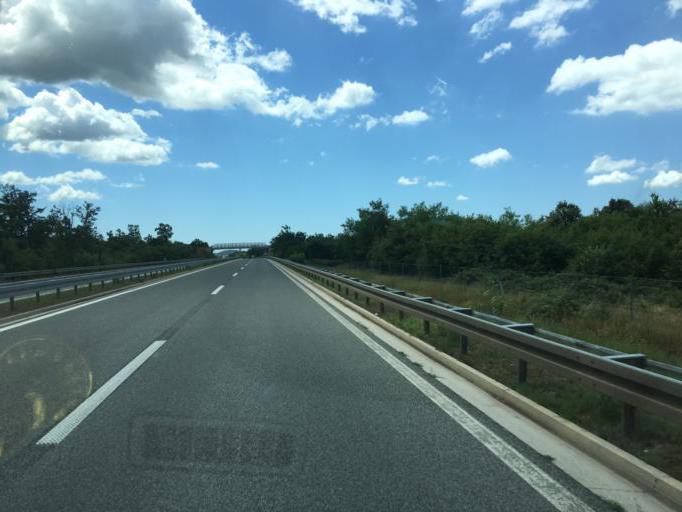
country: HR
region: Istarska
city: Vrsar
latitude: 45.1935
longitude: 13.7306
